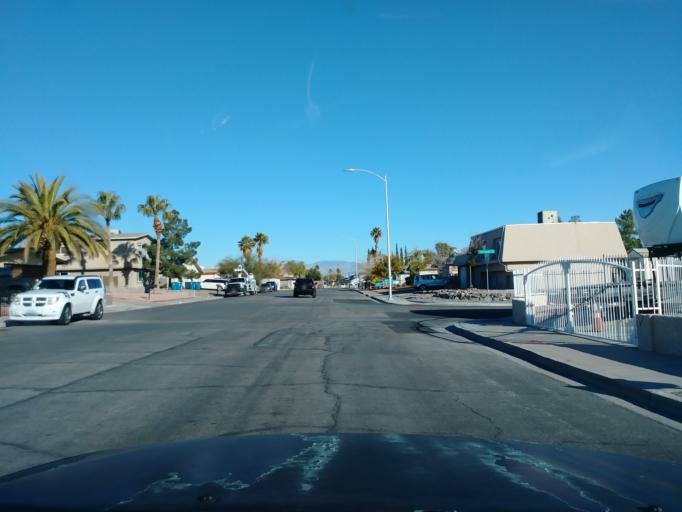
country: US
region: Nevada
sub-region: Clark County
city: Spring Valley
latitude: 36.1607
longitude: -115.2550
